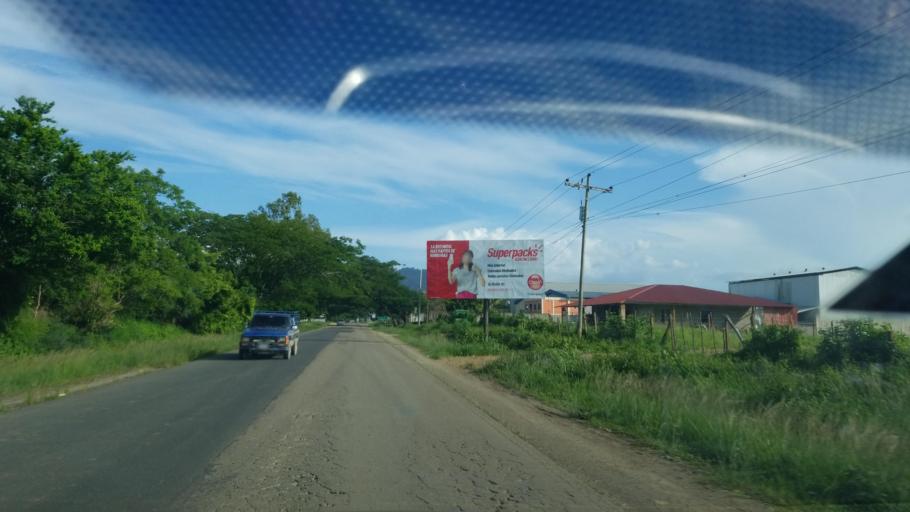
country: HN
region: El Paraiso
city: Cuyali
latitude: 13.8988
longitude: -86.5556
